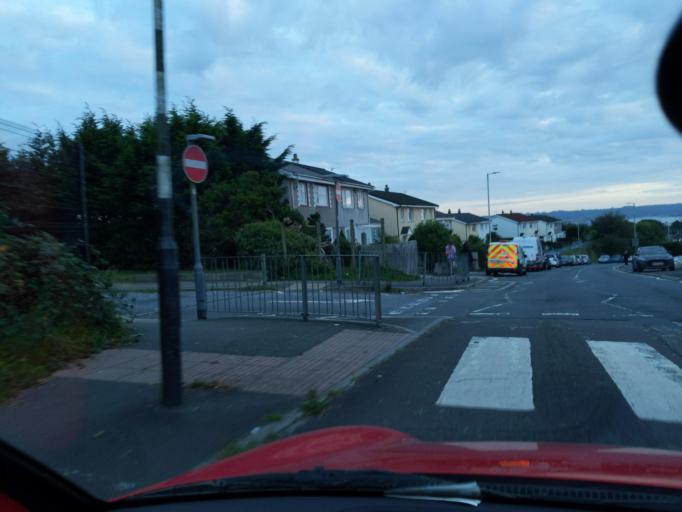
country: GB
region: England
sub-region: Cornwall
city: Torpoint
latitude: 50.4068
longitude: -4.1771
